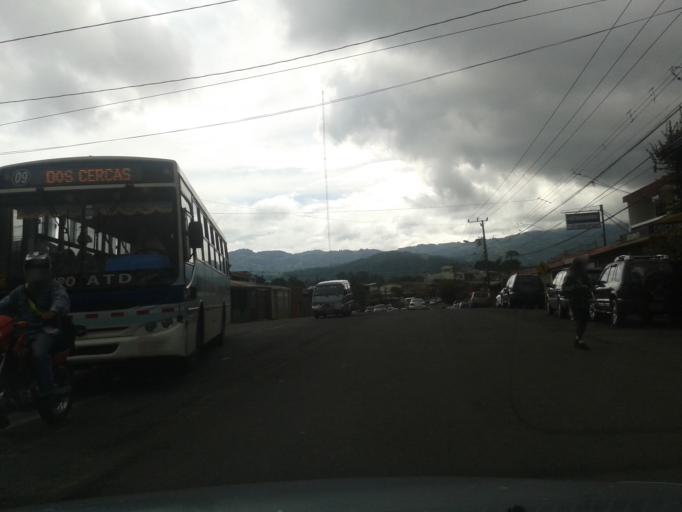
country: CR
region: San Jose
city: San Miguel
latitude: 9.8946
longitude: -84.0568
